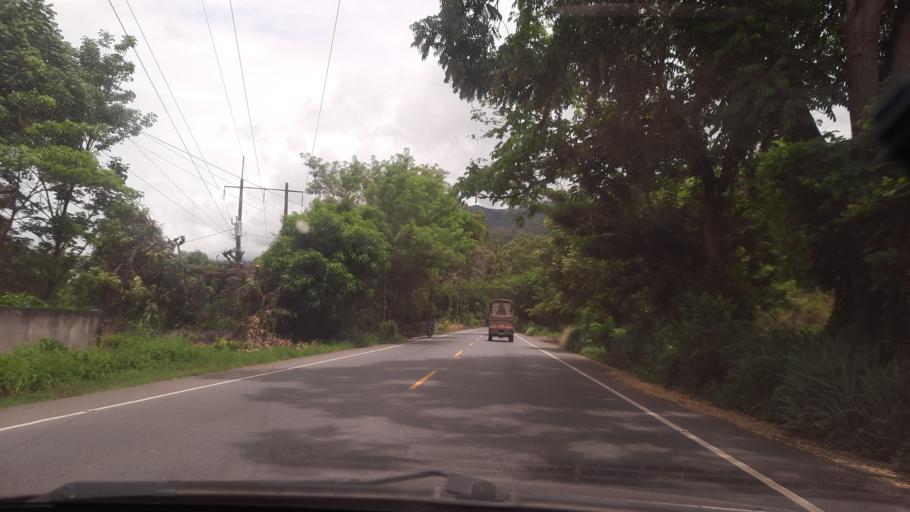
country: GT
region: Zacapa
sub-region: Municipio de Zacapa
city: Gualan
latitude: 15.1973
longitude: -89.2700
